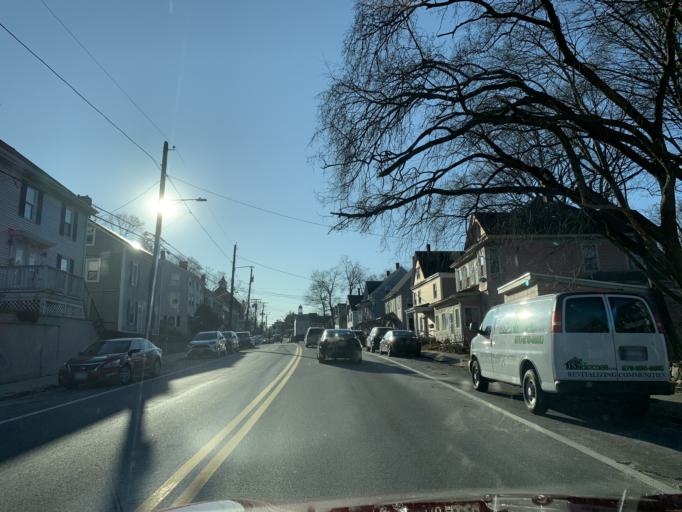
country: US
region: Massachusetts
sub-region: Essex County
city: Andover
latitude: 42.6598
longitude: -71.1432
